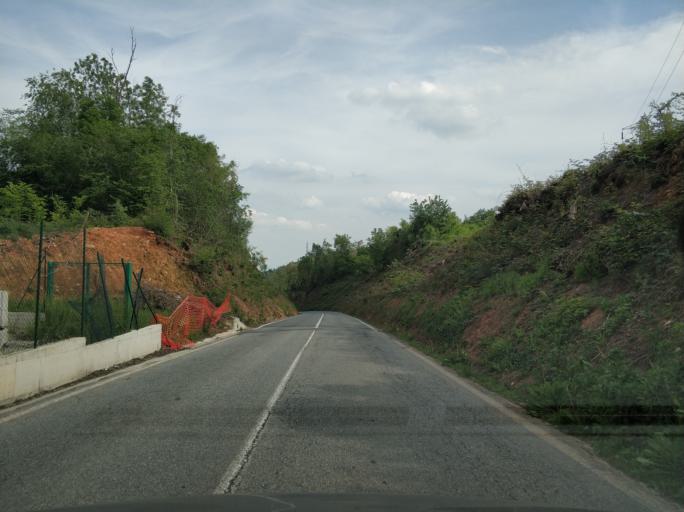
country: IT
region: Piedmont
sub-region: Provincia di Torino
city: Corio
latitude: 45.3052
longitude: 7.5385
